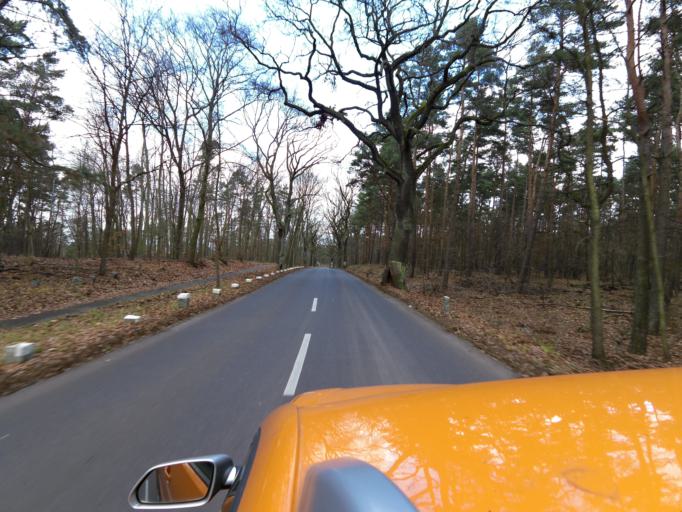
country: DE
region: Berlin
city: Gatow
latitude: 52.4894
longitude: 13.2050
